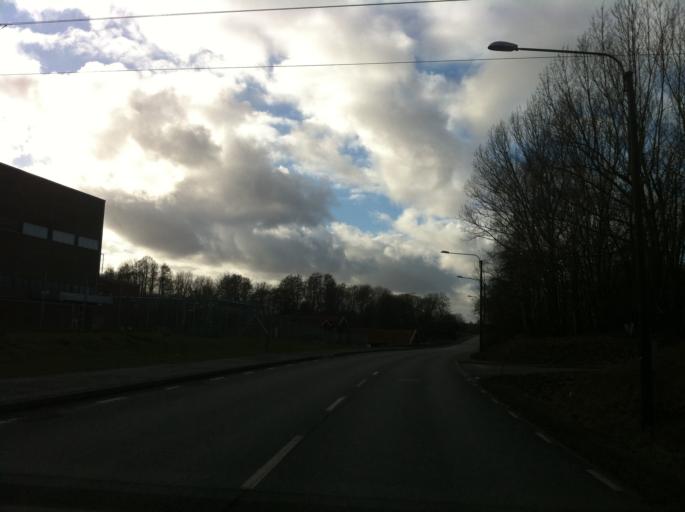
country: SE
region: Blekinge
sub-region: Solvesborgs Kommun
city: Soelvesborg
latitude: 56.0625
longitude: 14.5325
